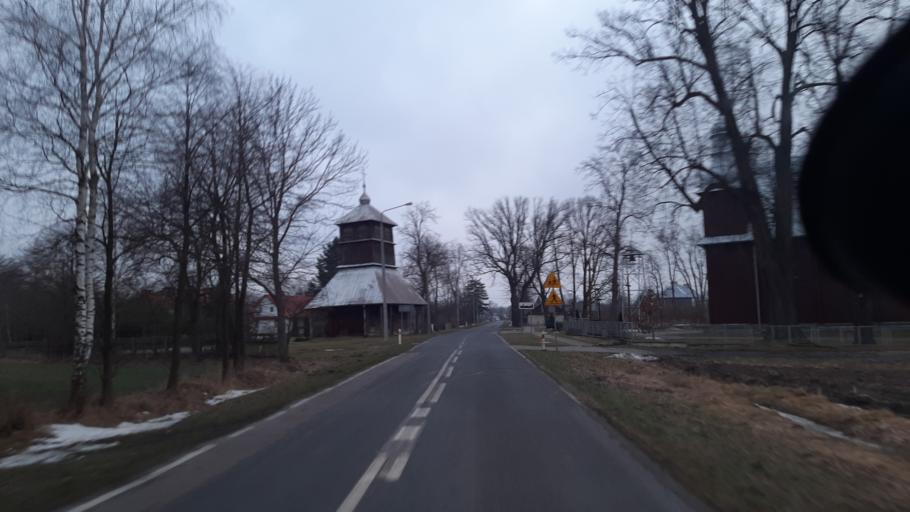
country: PL
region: Lublin Voivodeship
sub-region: Powiat parczewski
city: Sosnowica
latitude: 51.6042
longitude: 23.1313
